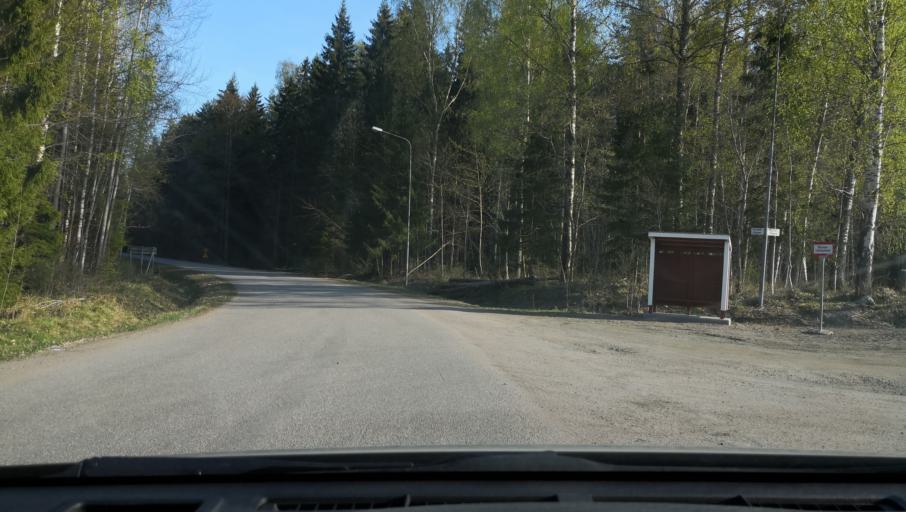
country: SE
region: Uppsala
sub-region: Heby Kommun
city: Tarnsjo
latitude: 60.2834
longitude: 16.8831
